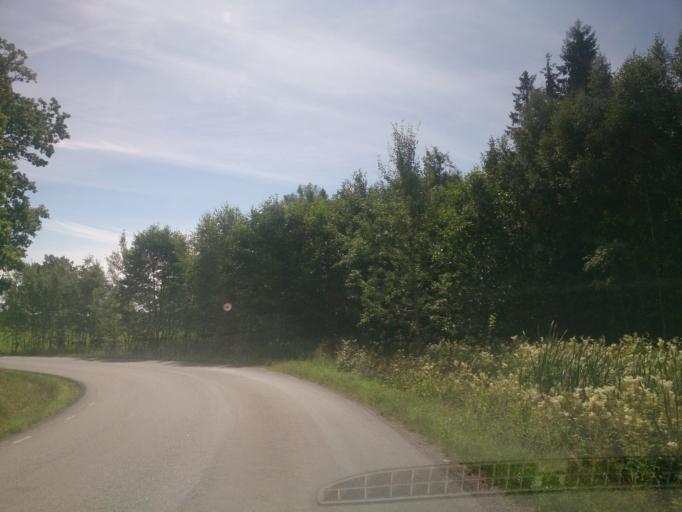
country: SE
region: OEstergoetland
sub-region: Valdemarsviks Kommun
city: Gusum
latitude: 58.2857
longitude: 16.5292
